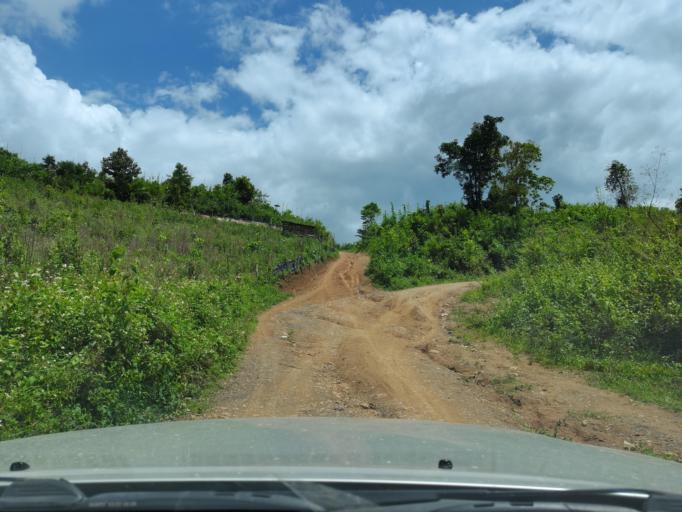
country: LA
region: Loungnamtha
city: Muang Long
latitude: 20.7296
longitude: 101.0145
